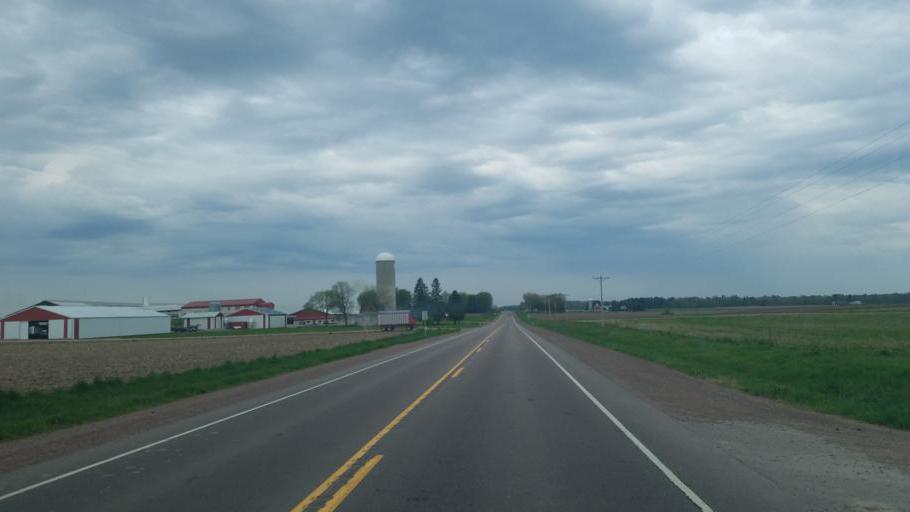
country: US
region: Wisconsin
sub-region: Wood County
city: Marshfield
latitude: 44.5989
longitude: -90.3019
